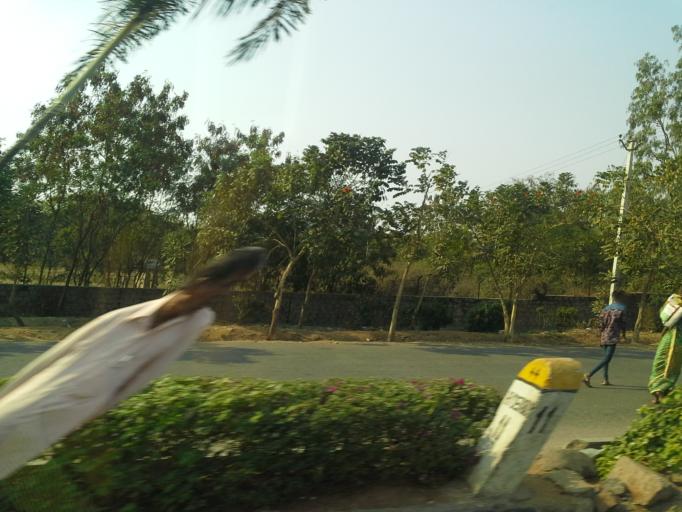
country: IN
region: Telangana
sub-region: Rangareddi
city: Balapur
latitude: 17.3108
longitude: 78.4232
